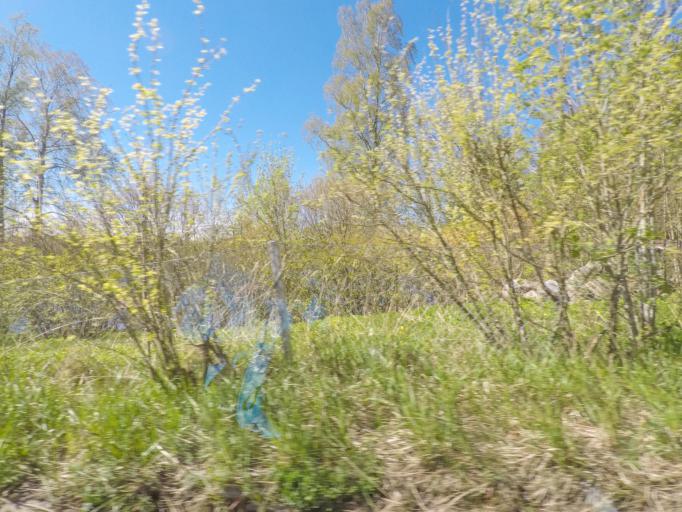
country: FI
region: Uusimaa
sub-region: Helsinki
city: Sammatti
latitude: 60.3422
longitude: 23.8022
